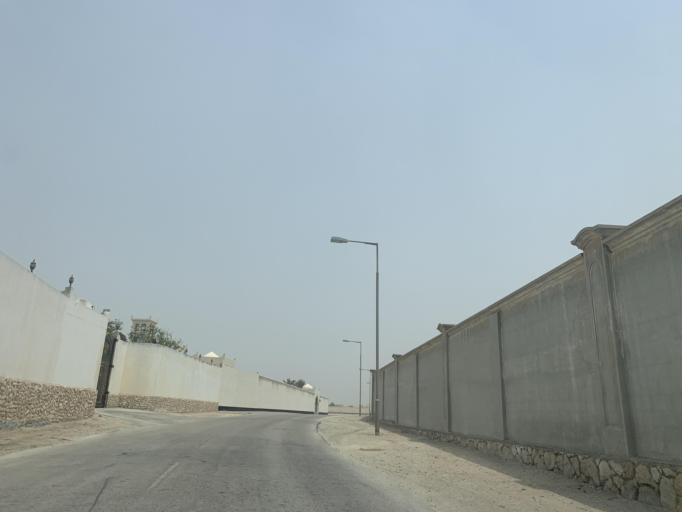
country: BH
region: Central Governorate
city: Madinat Hamad
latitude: 26.1623
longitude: 50.4807
